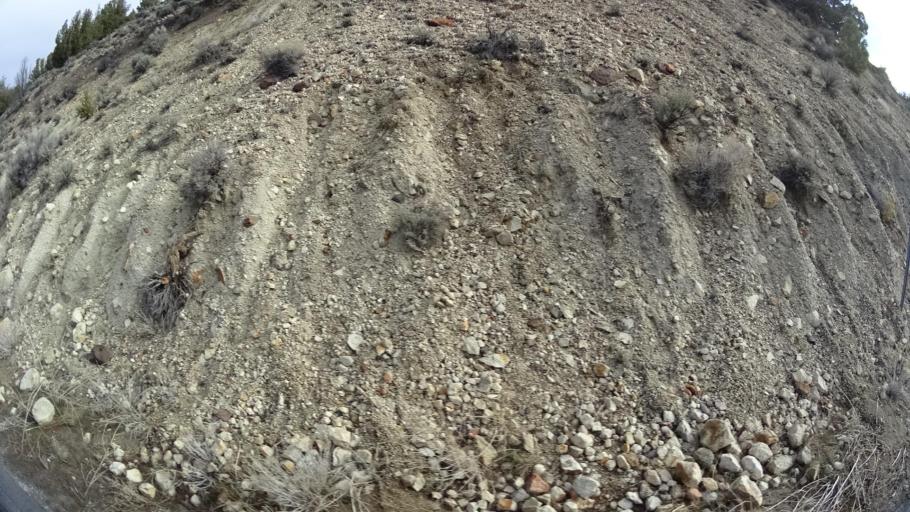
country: US
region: Nevada
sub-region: Washoe County
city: Cold Springs
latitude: 39.9035
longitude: -119.9983
